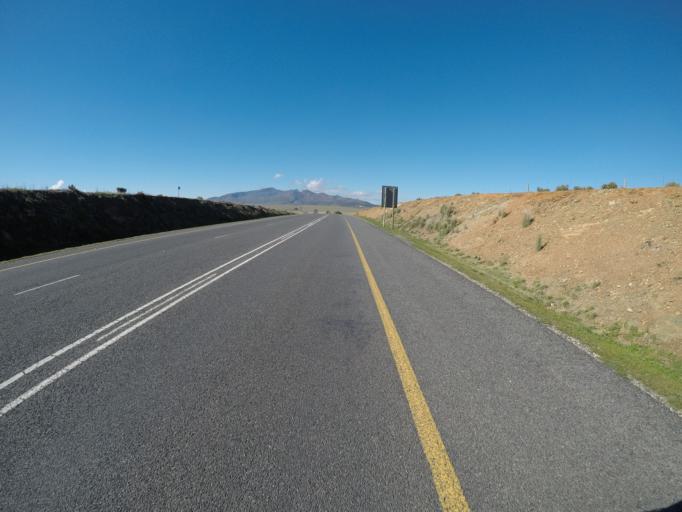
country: ZA
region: Western Cape
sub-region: Overberg District Municipality
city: Caledon
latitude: -34.2121
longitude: 19.3553
